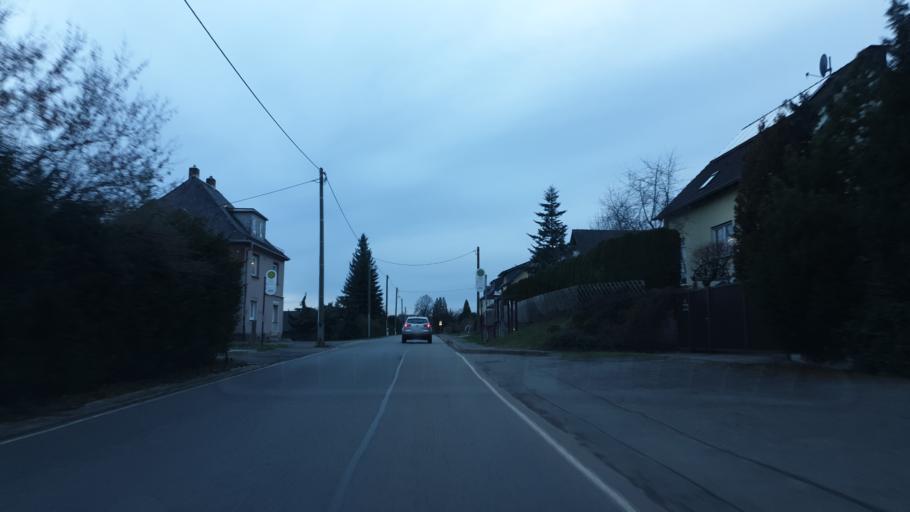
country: DE
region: Saxony
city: Hartenstein
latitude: 50.6787
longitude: 12.6672
